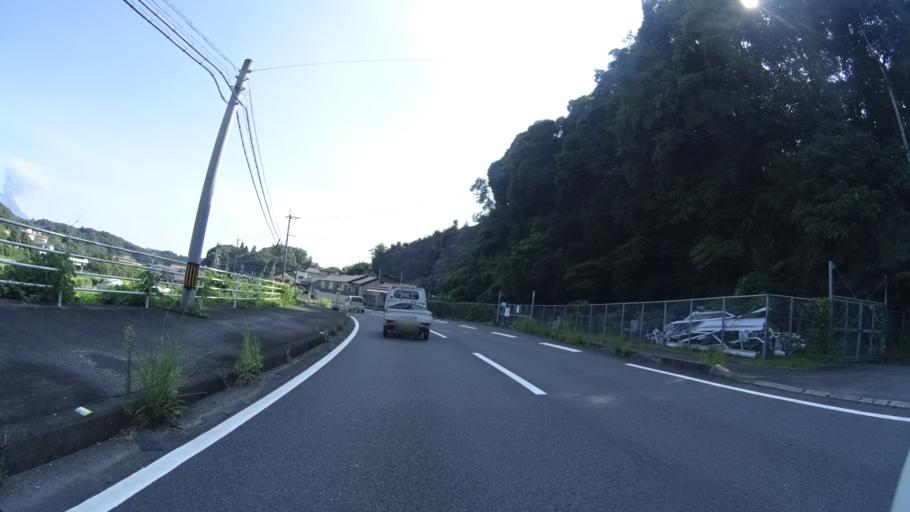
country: JP
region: Kagoshima
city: Kagoshima-shi
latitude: 31.6570
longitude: 130.5498
